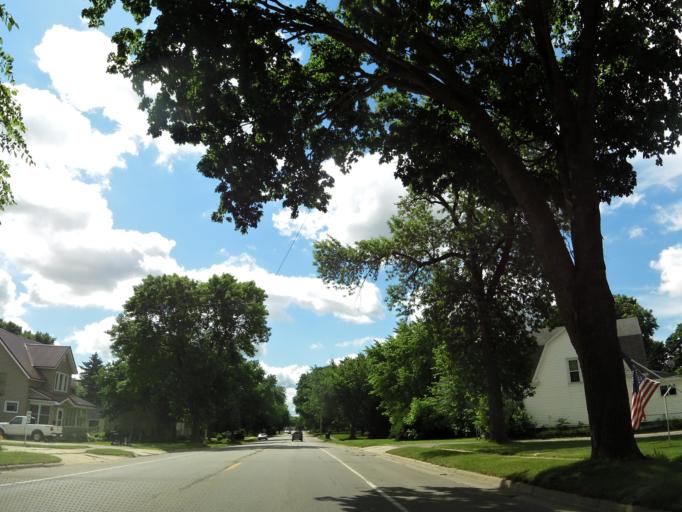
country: US
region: Minnesota
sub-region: Fillmore County
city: Spring Valley
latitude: 43.6940
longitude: -92.3943
